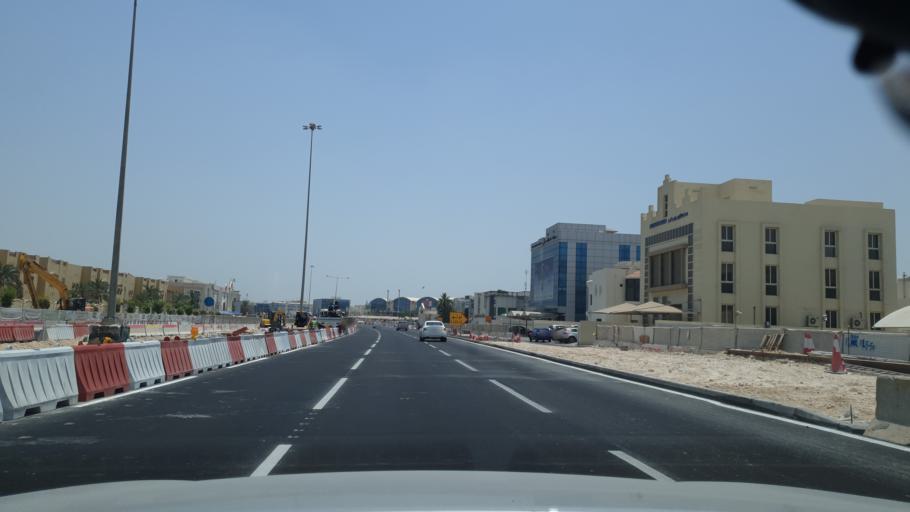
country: QA
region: Baladiyat ad Dawhah
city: Doha
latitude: 25.2537
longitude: 51.5413
